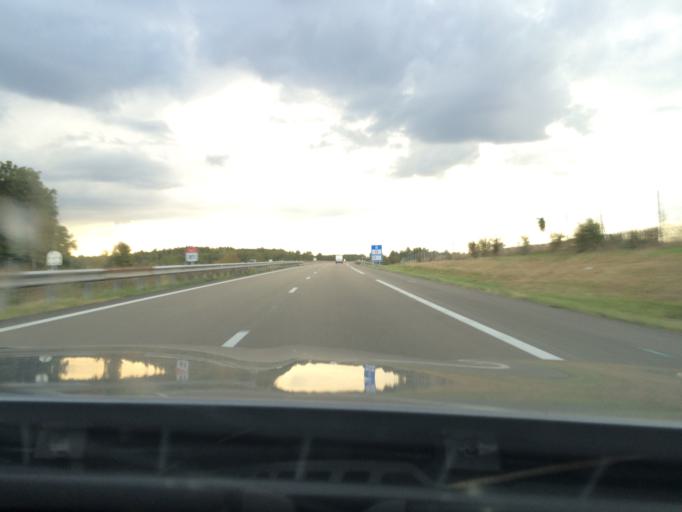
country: FR
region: Ile-de-France
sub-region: Departement de Seine-et-Marne
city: Souppes-sur-Loing
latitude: 48.2141
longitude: 2.7792
